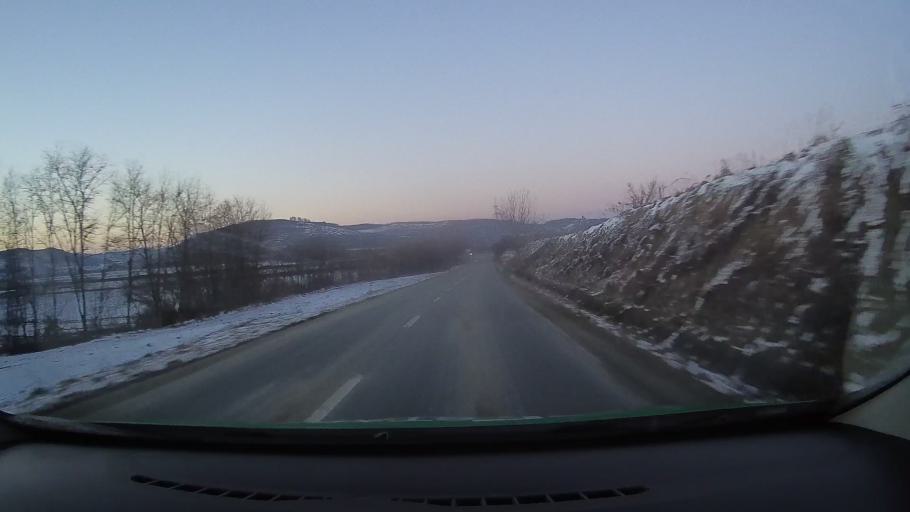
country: RO
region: Sibiu
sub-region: Comuna Alma
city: Alma
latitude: 46.1911
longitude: 24.4706
